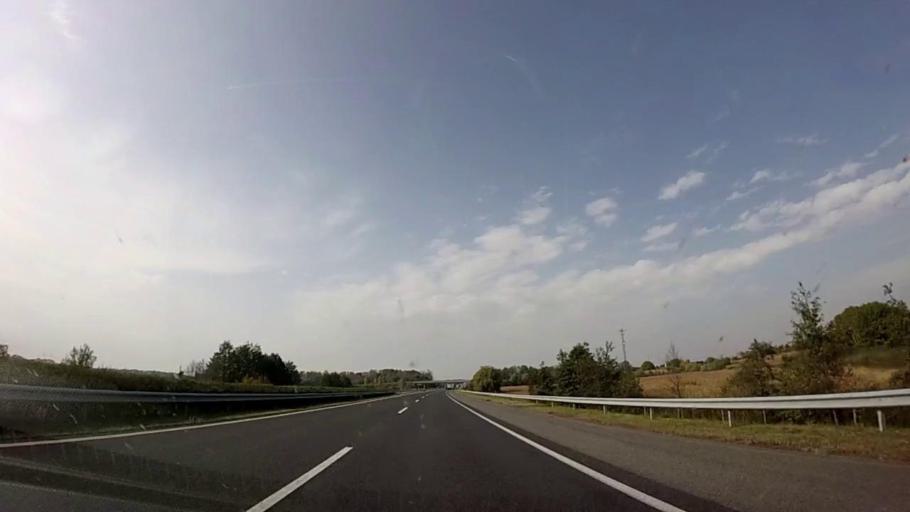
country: HU
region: Zala
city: Letenye
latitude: 46.4166
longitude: 16.7579
